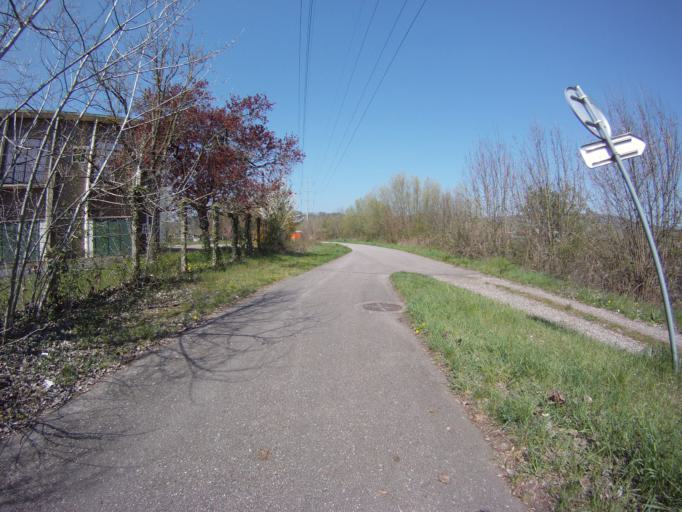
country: FR
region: Lorraine
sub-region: Departement de Meurthe-et-Moselle
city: Custines
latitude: 48.7871
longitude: 6.1403
